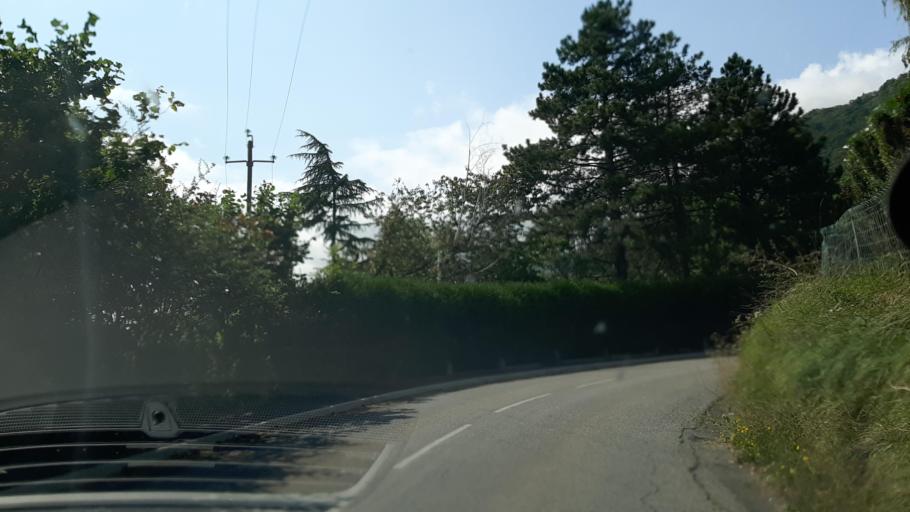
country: FR
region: Rhone-Alpes
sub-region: Departement de la Savoie
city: Mercury
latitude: 45.6696
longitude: 6.3309
